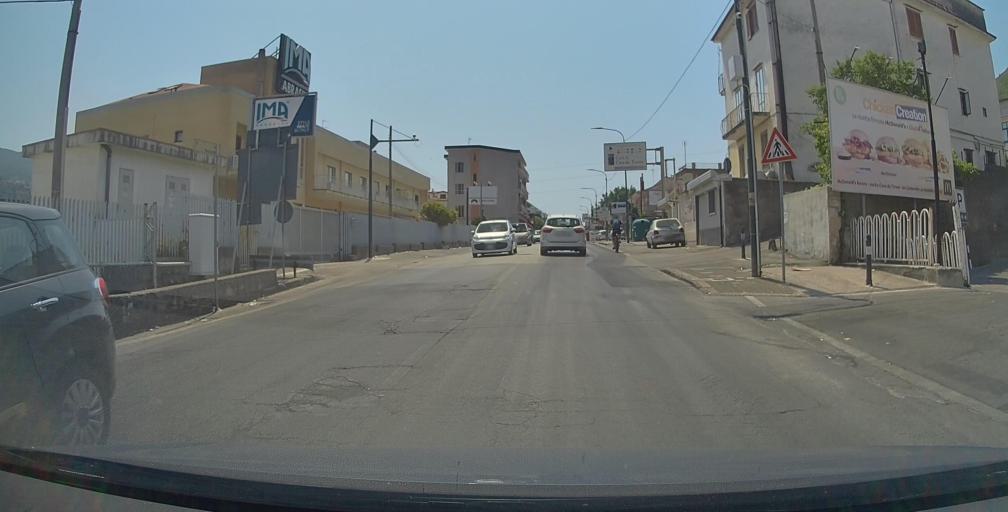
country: IT
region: Campania
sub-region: Provincia di Salerno
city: Nocera Superiore
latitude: 40.7282
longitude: 14.6904
